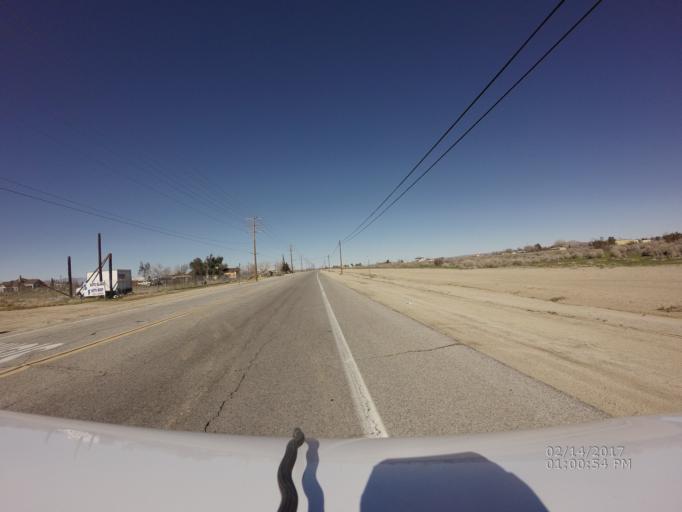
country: US
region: California
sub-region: Los Angeles County
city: Littlerock
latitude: 34.5811
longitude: -117.9694
